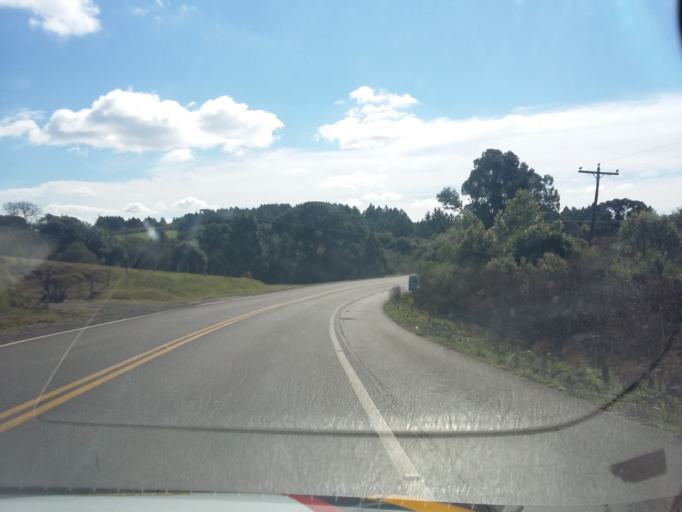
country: BR
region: Rio Grande do Sul
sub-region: Sao Marcos
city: Sao Marcos
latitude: -28.7769
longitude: -51.0931
